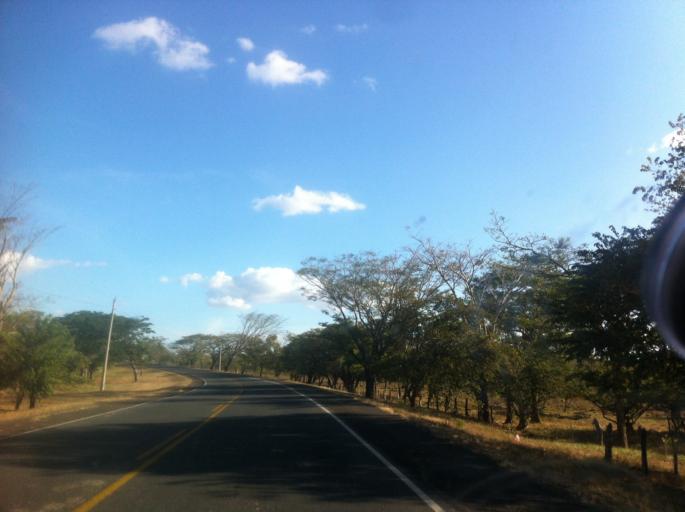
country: NI
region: Chontales
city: Acoyapa
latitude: 11.9308
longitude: -85.1426
